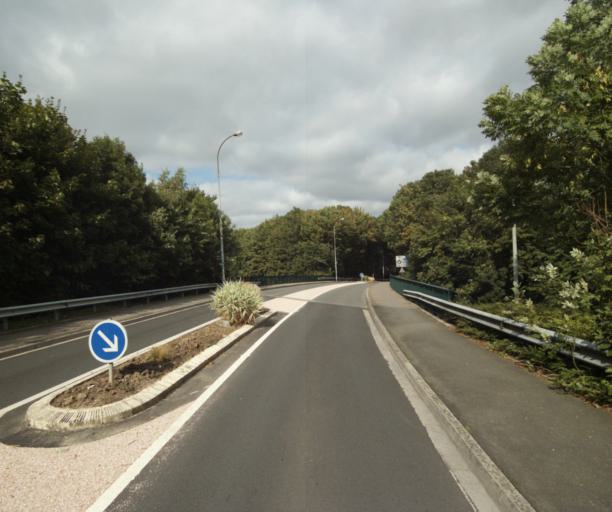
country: FR
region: Nord-Pas-de-Calais
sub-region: Departement du Nord
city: Lys-lez-Lannoy
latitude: 50.6731
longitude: 3.2236
